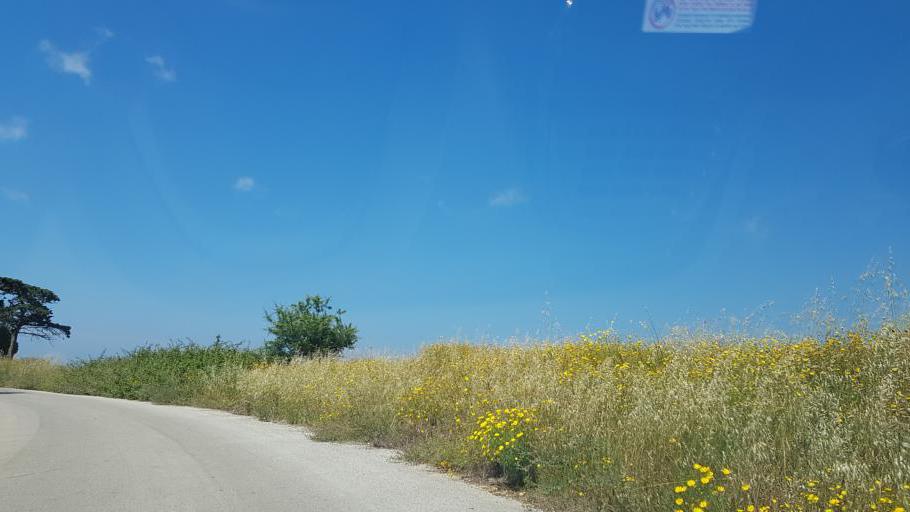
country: IT
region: Apulia
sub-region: Provincia di Brindisi
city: Brindisi
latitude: 40.6497
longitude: 17.8550
